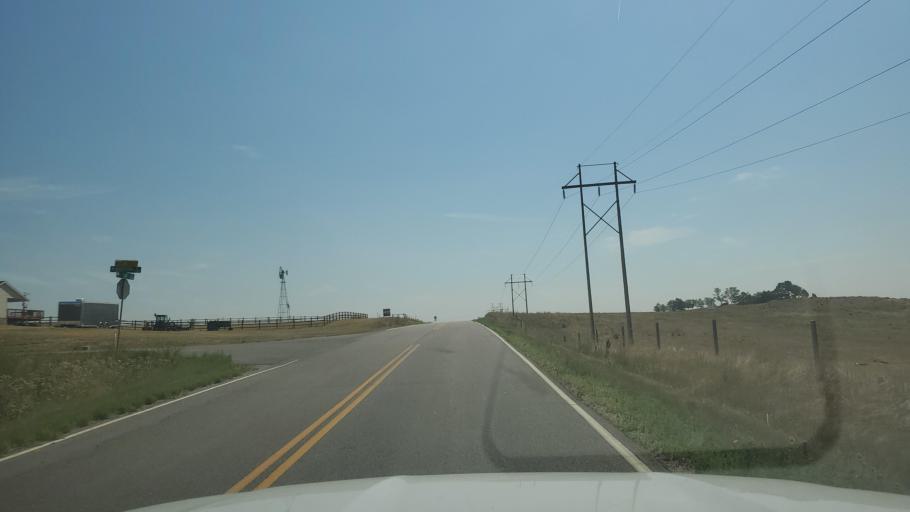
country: US
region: Colorado
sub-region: Adams County
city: Todd Creek
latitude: 39.9431
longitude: -104.8801
